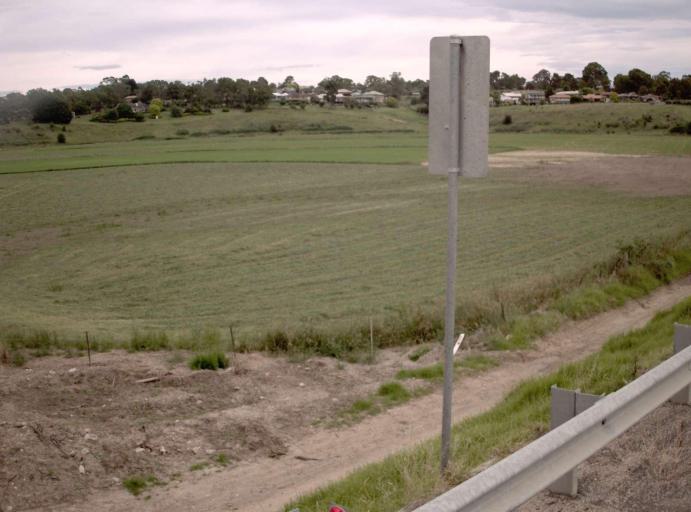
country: AU
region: Victoria
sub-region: East Gippsland
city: Bairnsdale
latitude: -37.8138
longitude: 147.6180
